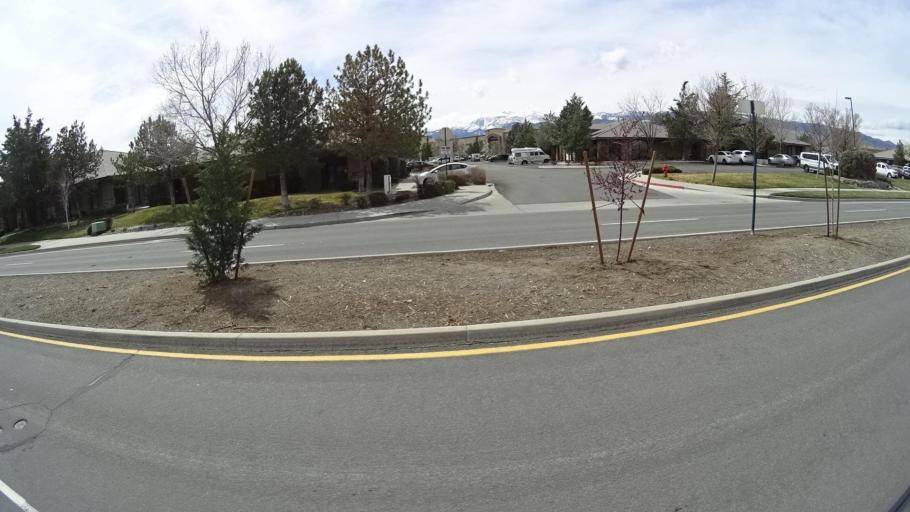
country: US
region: Nevada
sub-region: Washoe County
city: Sparks
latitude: 39.4312
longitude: -119.7545
